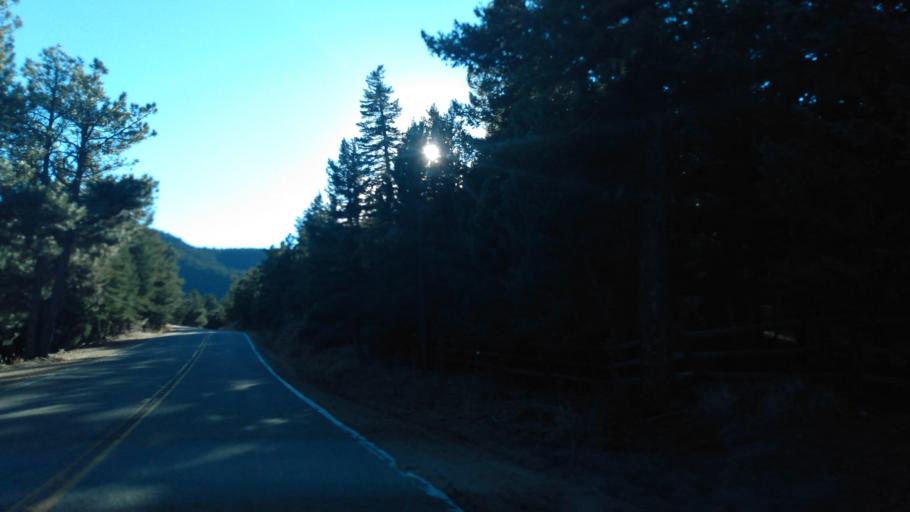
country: US
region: Colorado
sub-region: Boulder County
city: Coal Creek
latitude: 39.9914
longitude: -105.3693
